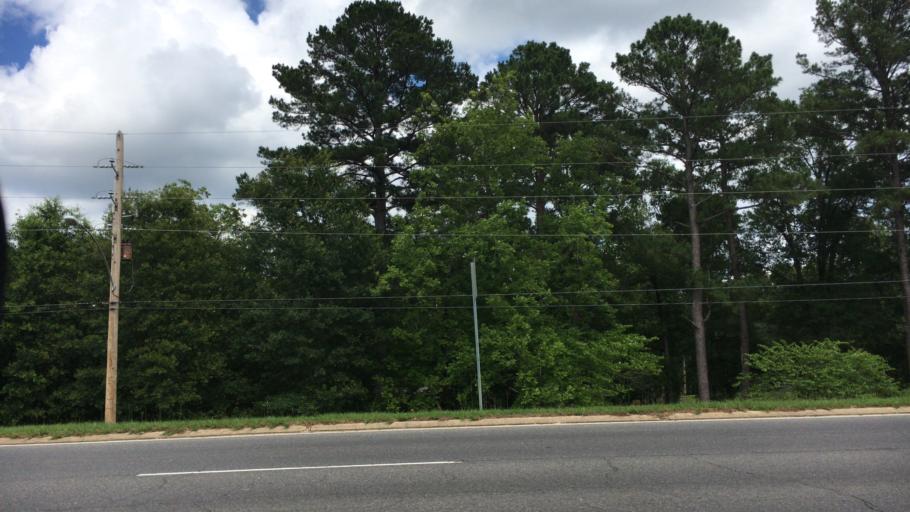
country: US
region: Louisiana
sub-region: Lincoln Parish
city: Ruston
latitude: 32.4973
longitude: -92.6367
